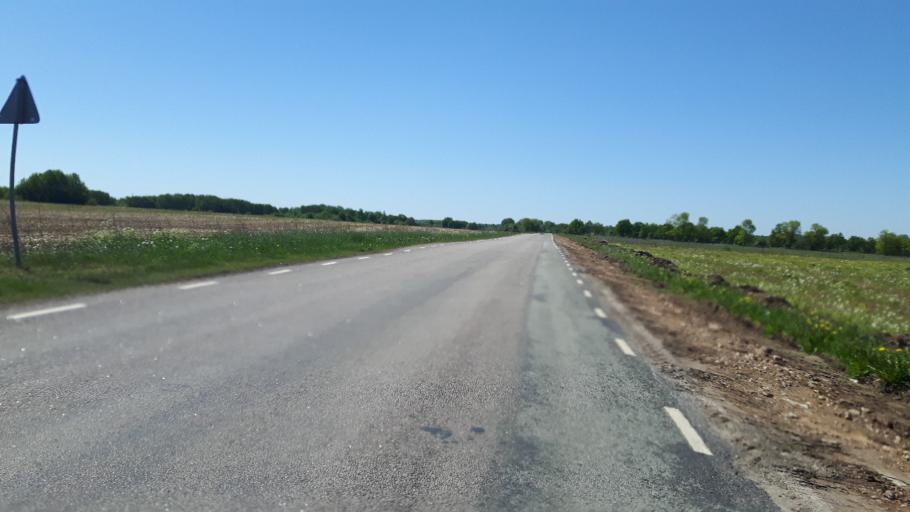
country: EE
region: Ida-Virumaa
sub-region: Narva-Joesuu linn
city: Narva-Joesuu
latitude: 59.4002
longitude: 27.9341
